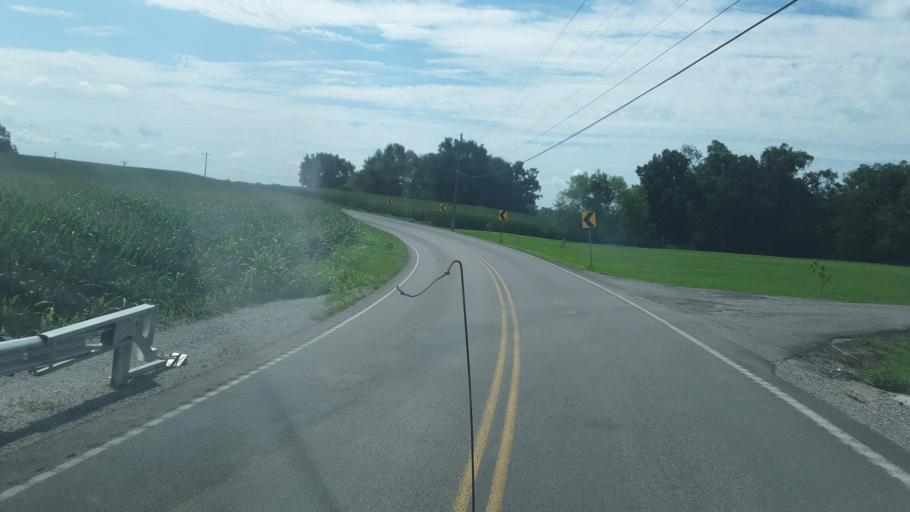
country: US
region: Kentucky
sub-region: Christian County
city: Oak Grove
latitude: 36.7555
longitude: -87.3198
